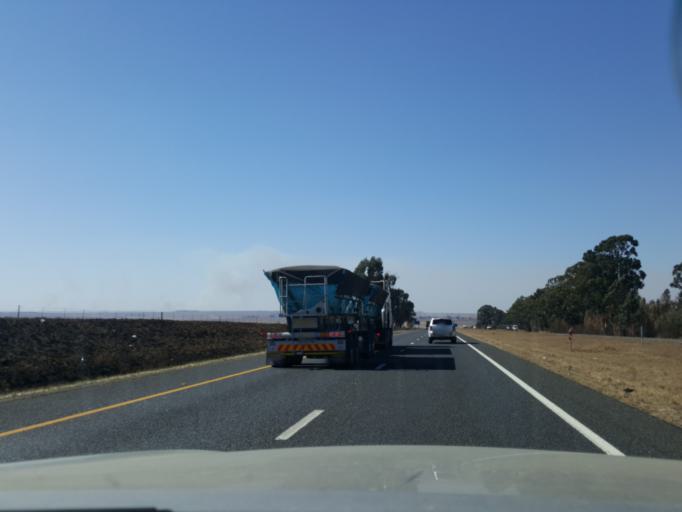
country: ZA
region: Mpumalanga
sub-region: Nkangala District Municipality
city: Delmas
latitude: -26.0402
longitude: 28.8437
